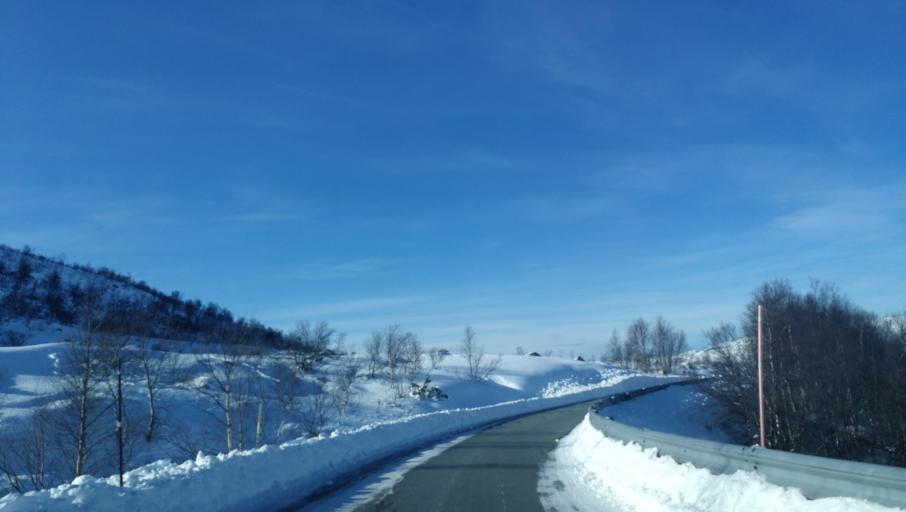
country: NO
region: Rogaland
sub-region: Hjelmeland
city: Hjelmelandsvagen
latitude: 59.1042
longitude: 6.3791
